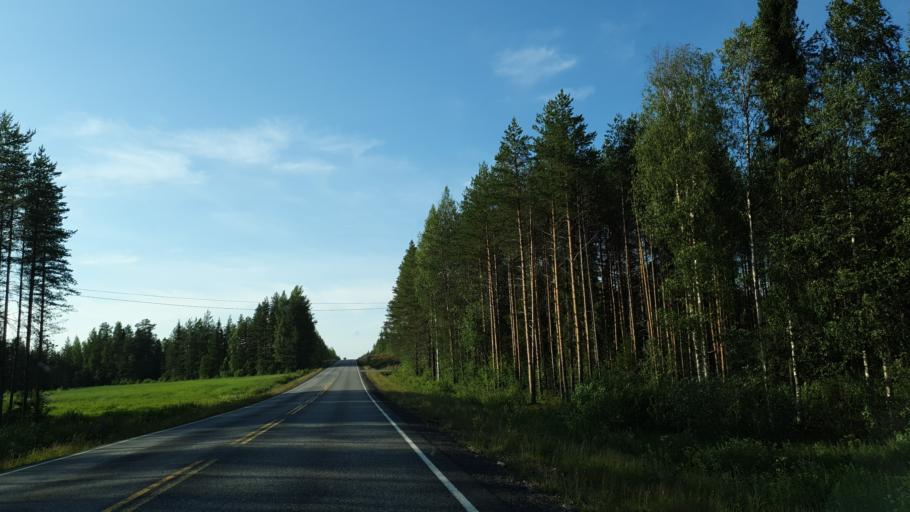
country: FI
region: Kainuu
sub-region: Kehys-Kainuu
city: Kuhmo
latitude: 64.0817
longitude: 29.4853
